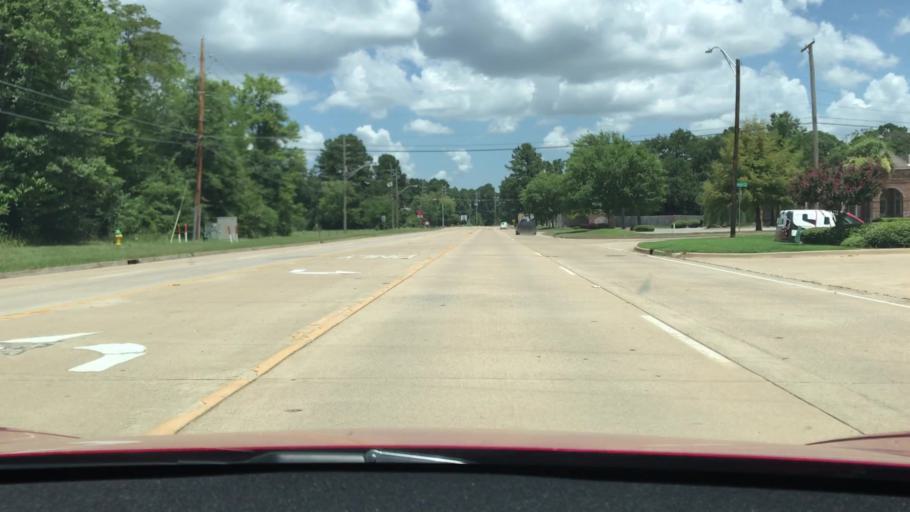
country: US
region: Louisiana
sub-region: Bossier Parish
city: Bossier City
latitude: 32.4101
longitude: -93.7384
